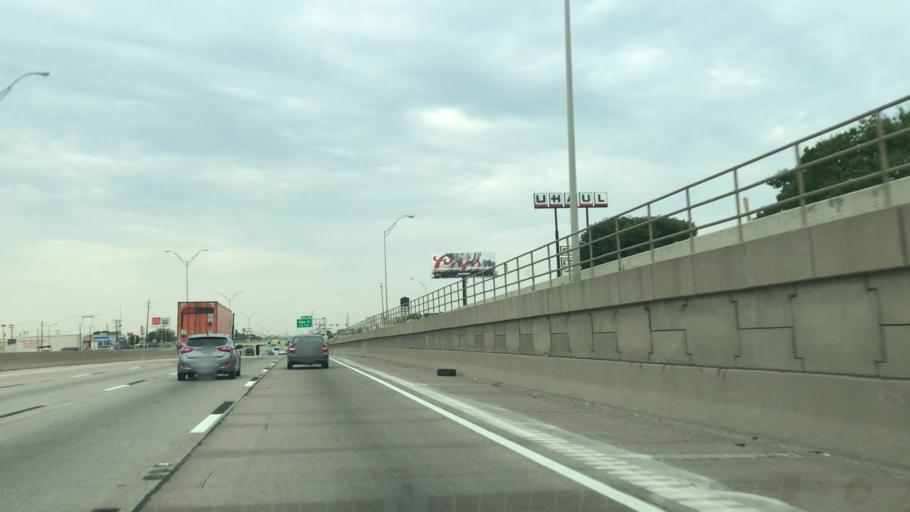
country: US
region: Texas
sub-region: Tarrant County
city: Fort Worth
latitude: 32.7094
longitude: -97.3208
